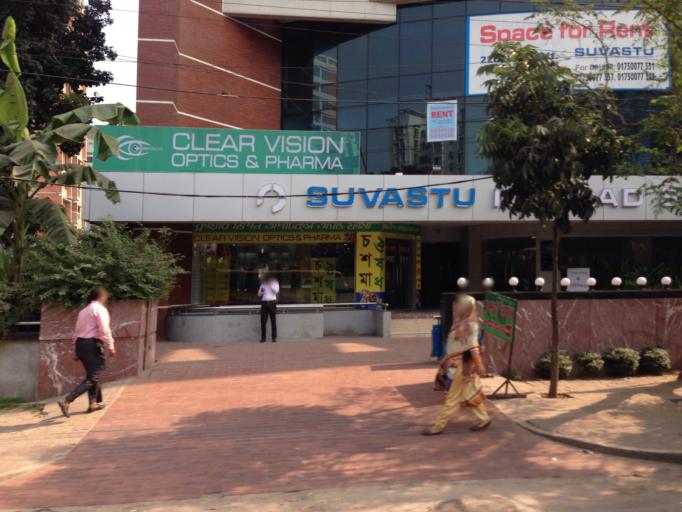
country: BD
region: Dhaka
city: Azimpur
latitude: 23.7428
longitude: 90.3828
